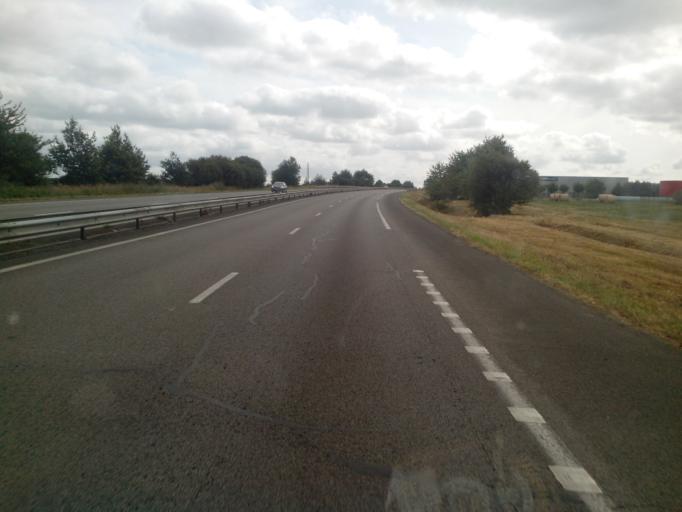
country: FR
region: Pays de la Loire
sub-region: Departement de la Loire-Atlantique
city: Heric
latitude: 47.3715
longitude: -1.6455
